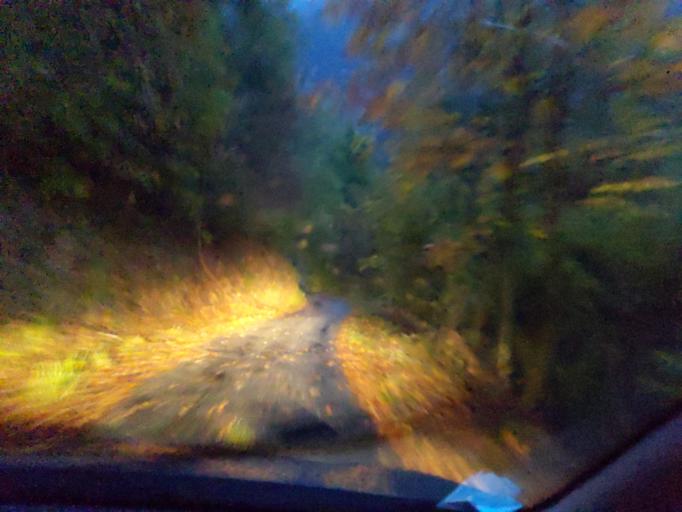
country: FR
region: Rhone-Alpes
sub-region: Departement de la Savoie
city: Aiton
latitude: 45.5198
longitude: 6.3316
